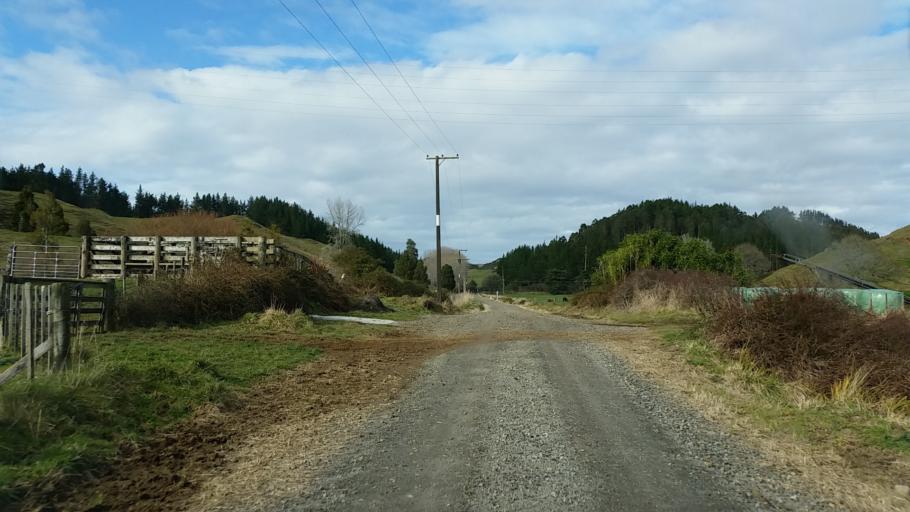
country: NZ
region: Taranaki
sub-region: South Taranaki District
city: Eltham
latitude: -39.2294
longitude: 174.5652
